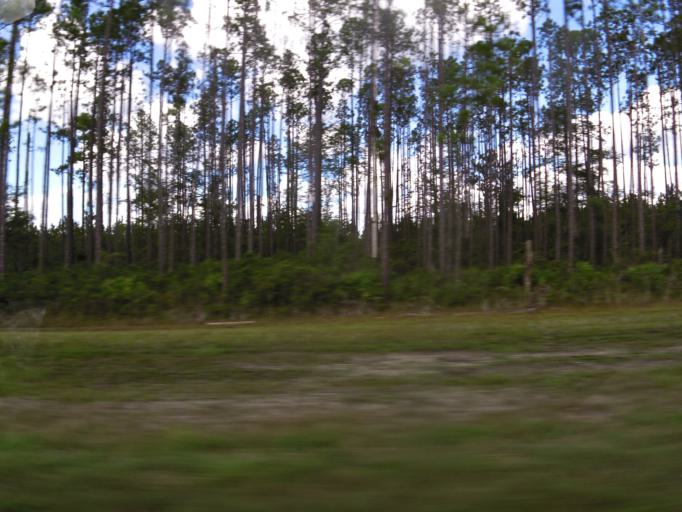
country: US
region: Florida
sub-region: Hamilton County
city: Jasper
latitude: 30.6764
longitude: -82.6944
